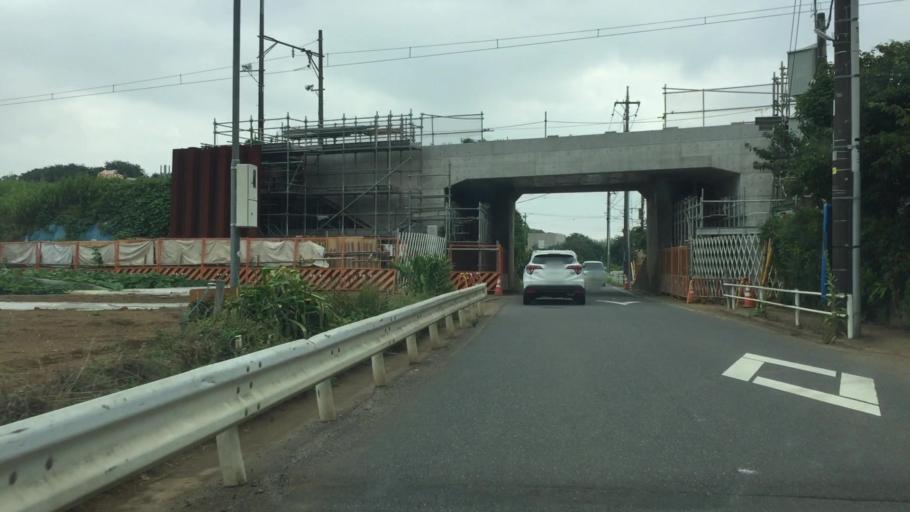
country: JP
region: Chiba
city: Kashiwa
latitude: 35.8195
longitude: 139.9887
